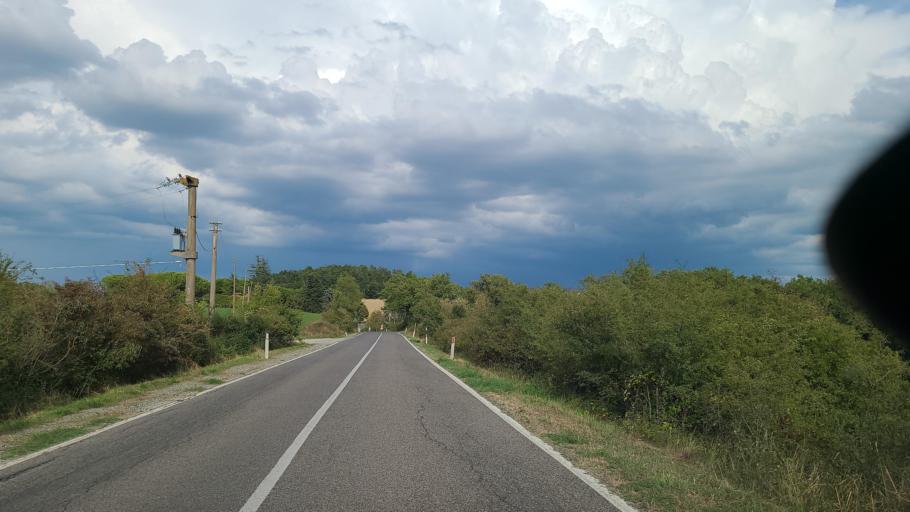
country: IT
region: Tuscany
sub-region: Province of Florence
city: Gambassi Terme
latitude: 43.4850
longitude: 10.9685
